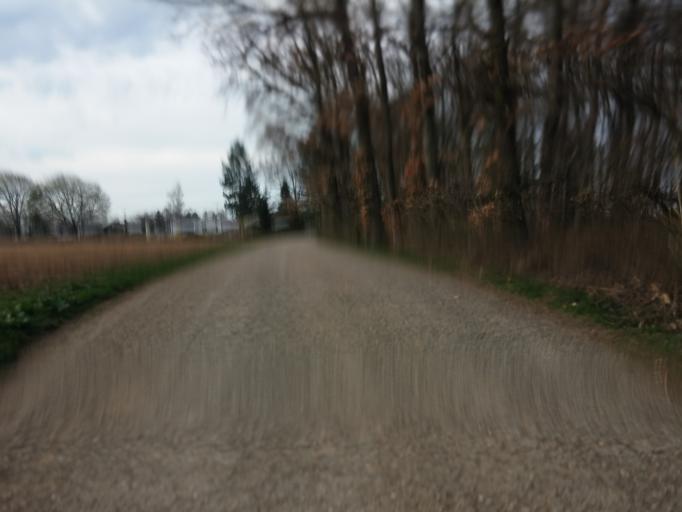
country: DE
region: Bavaria
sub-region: Upper Bavaria
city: Haar
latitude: 48.1007
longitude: 11.7362
